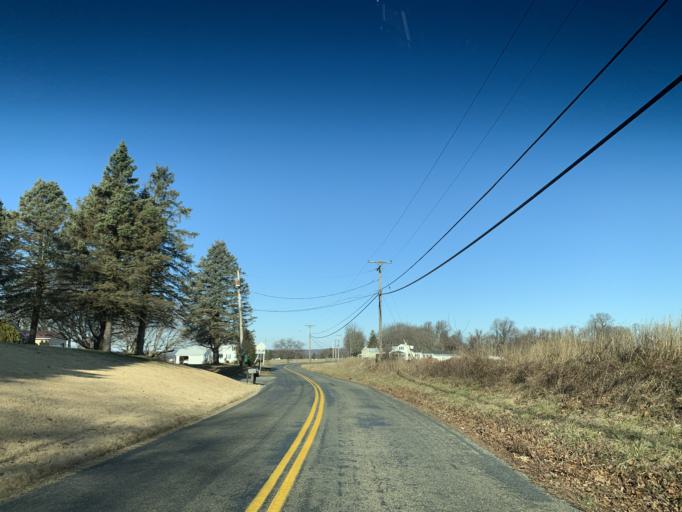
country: US
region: Maryland
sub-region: Harford County
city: Aberdeen
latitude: 39.5827
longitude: -76.1993
